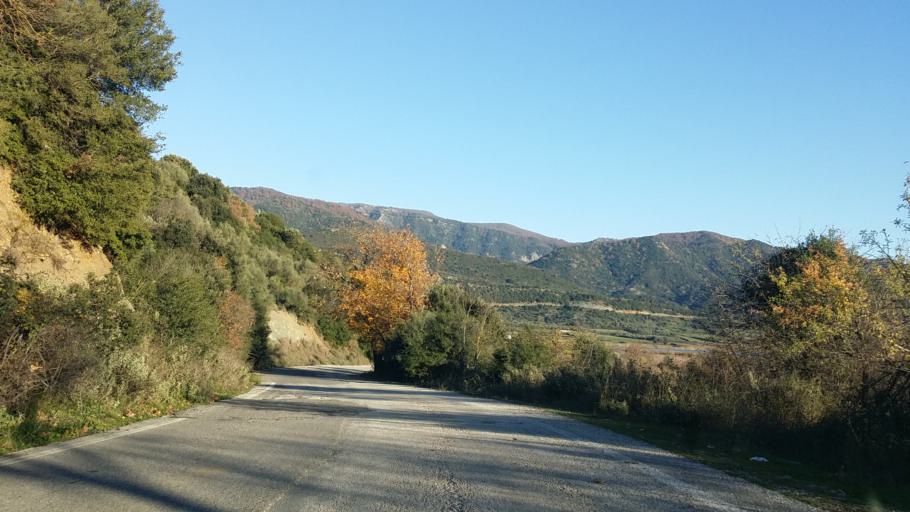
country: GR
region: West Greece
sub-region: Nomos Aitolias kai Akarnanias
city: Sardinia
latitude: 38.8517
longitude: 21.3352
